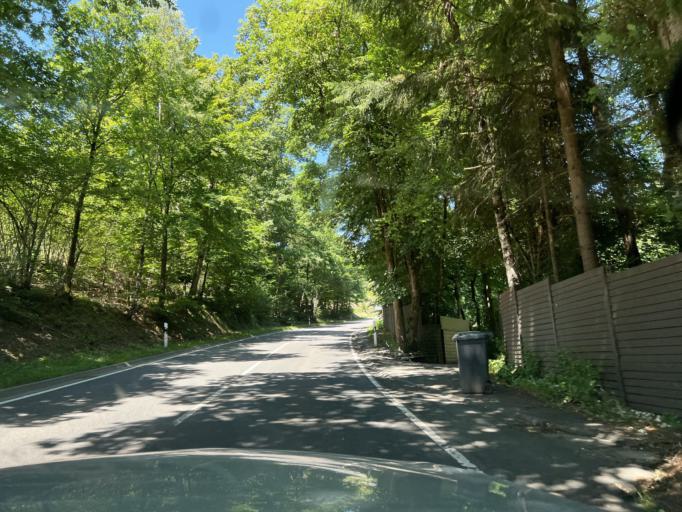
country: DE
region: North Rhine-Westphalia
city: Freudenberg
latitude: 50.9316
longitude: 7.9289
